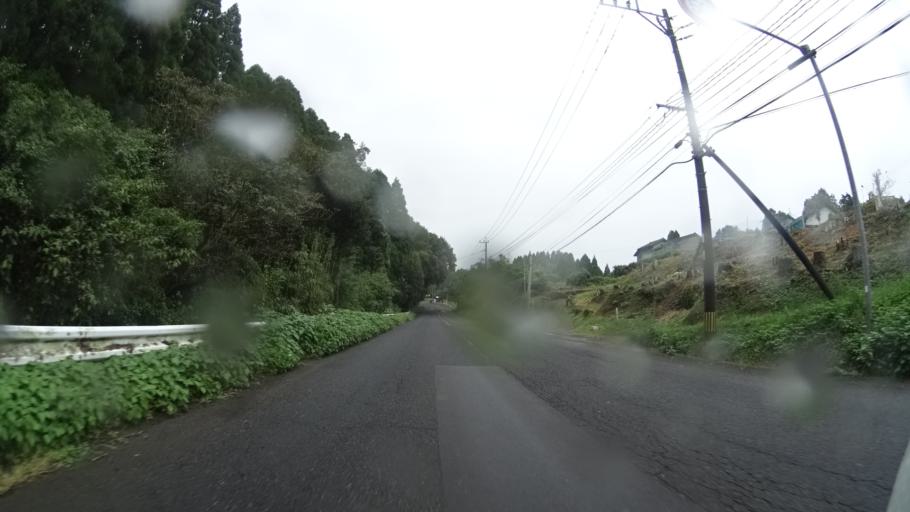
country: JP
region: Kagoshima
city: Kajiki
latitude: 31.7891
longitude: 130.6759
